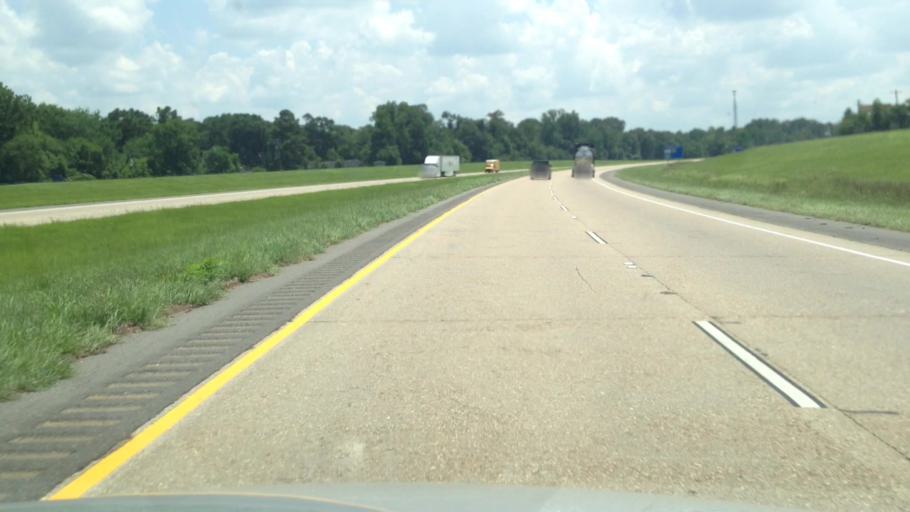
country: US
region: Louisiana
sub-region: Saint Landry Parish
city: Opelousas
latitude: 30.5488
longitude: -92.0533
